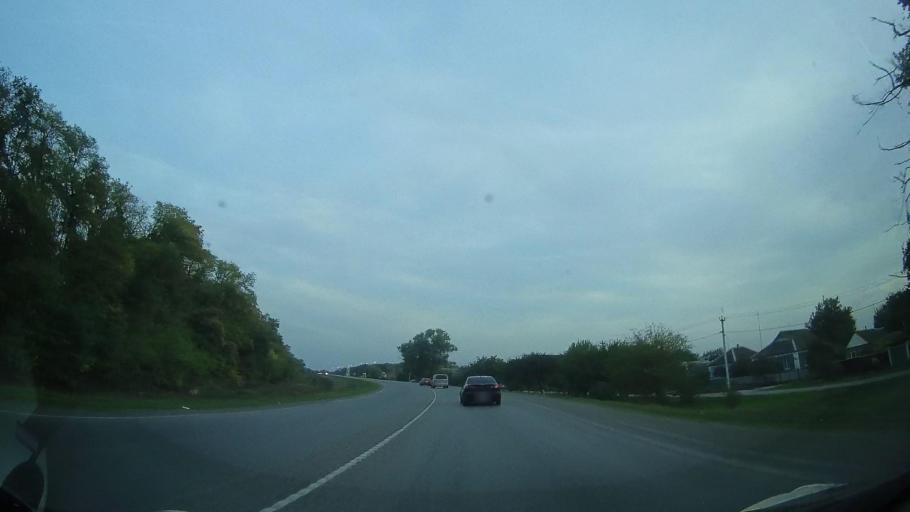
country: RU
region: Rostov
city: Kirovskaya
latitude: 46.9707
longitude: 40.0543
